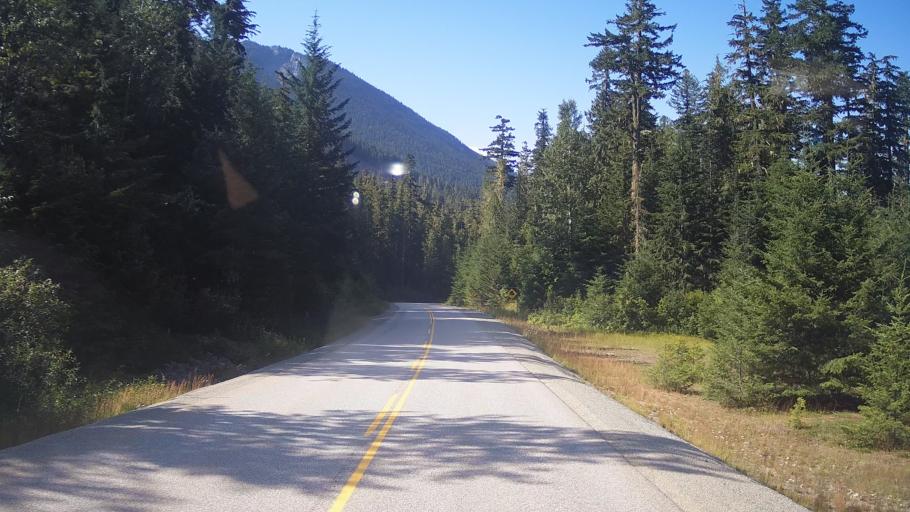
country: CA
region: British Columbia
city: Pemberton
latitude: 50.3478
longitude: -122.5339
